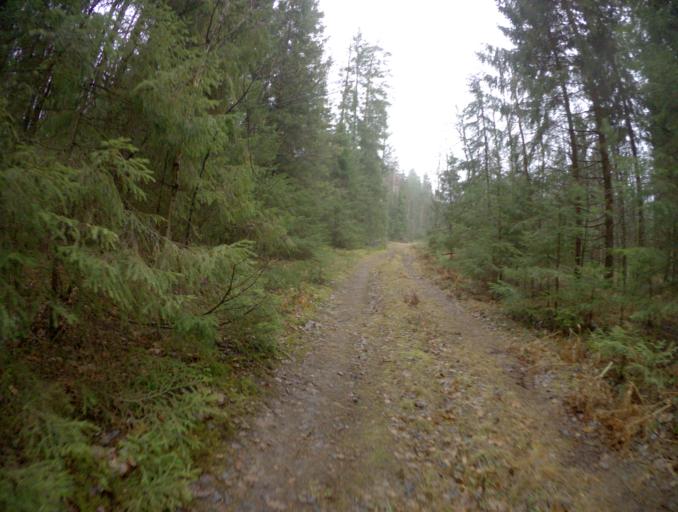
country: RU
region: Vladimir
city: Golovino
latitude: 56.0091
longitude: 40.4834
